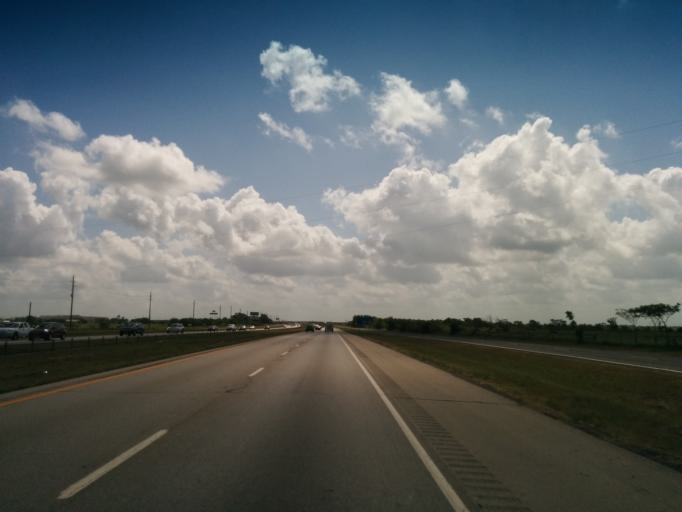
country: US
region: Texas
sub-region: Austin County
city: Sealy
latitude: 29.7568
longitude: -96.2325
